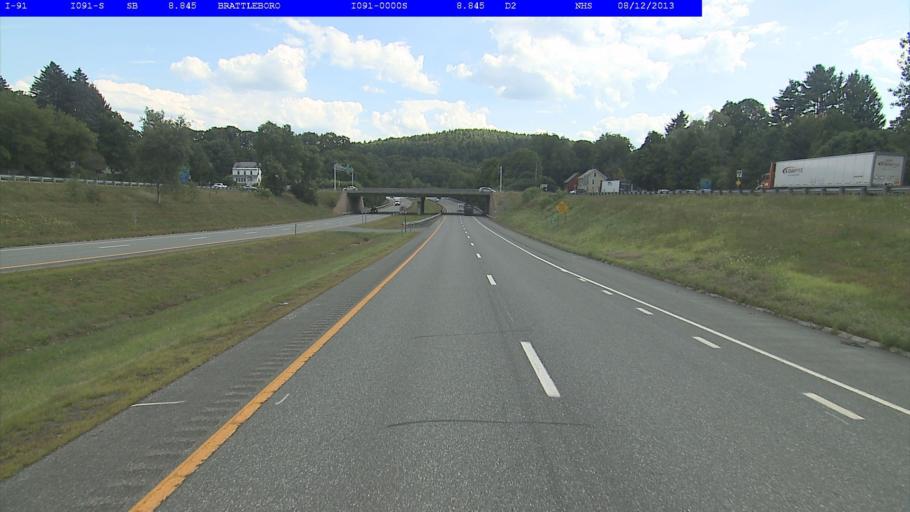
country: US
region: Vermont
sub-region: Windham County
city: Brattleboro
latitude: 42.8522
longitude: -72.5799
